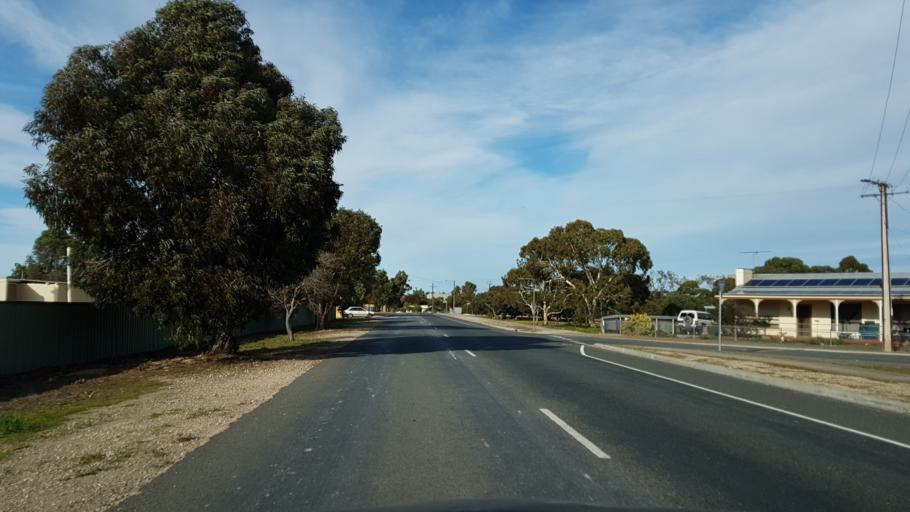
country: AU
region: South Australia
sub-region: Murray Bridge
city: Tailem Bend
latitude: -35.2483
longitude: 139.4551
